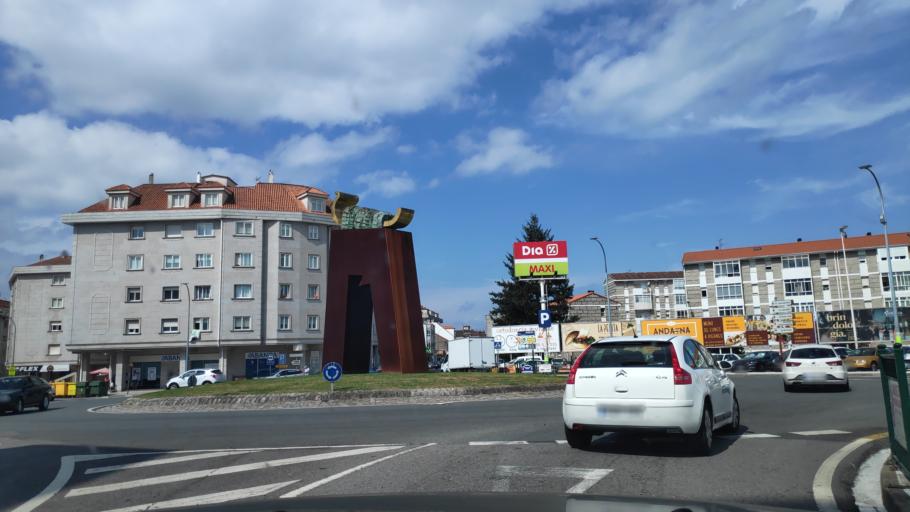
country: ES
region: Galicia
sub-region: Provincia de Pontevedra
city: Vilagarcia de Arousa
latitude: 42.5942
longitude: -8.7569
